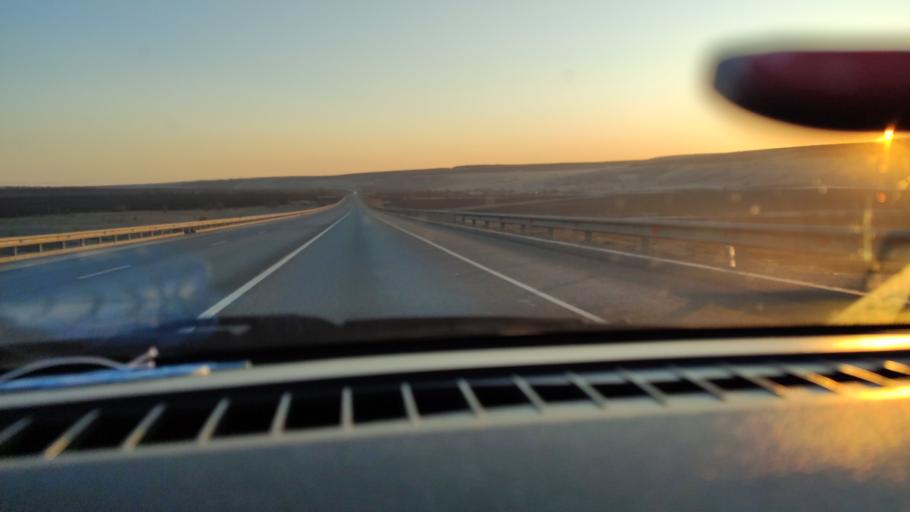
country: RU
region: Saratov
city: Yelshanka
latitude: 51.8404
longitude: 46.4778
